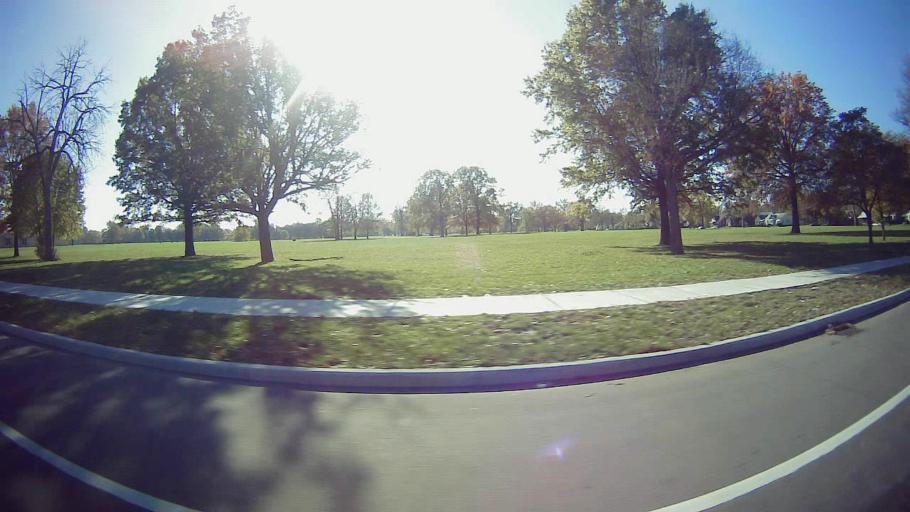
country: US
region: Michigan
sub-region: Wayne County
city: Dearborn
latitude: 42.3652
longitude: -83.2078
